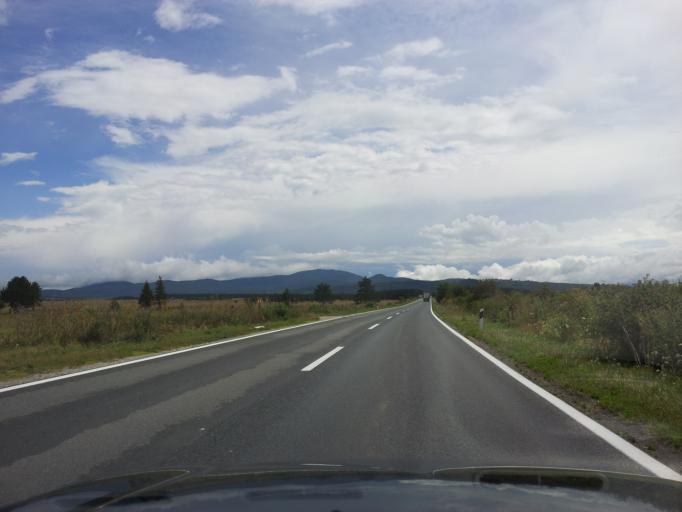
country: BA
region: Federation of Bosnia and Herzegovina
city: Bihac
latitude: 44.5711
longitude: 15.7528
